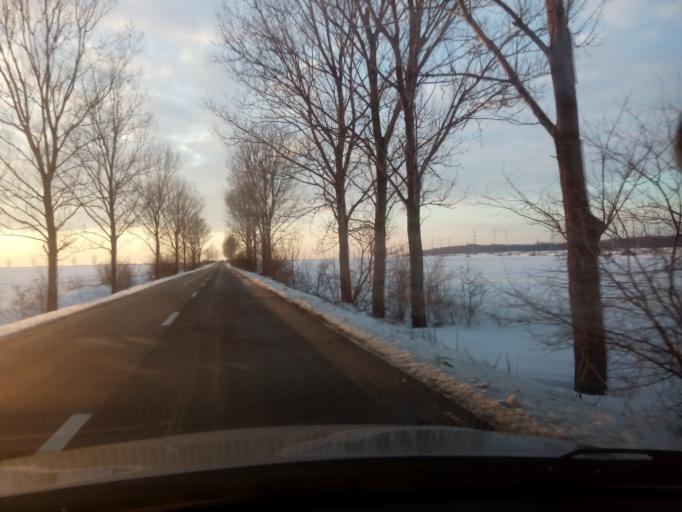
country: RO
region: Calarasi
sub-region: Comuna Luica
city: Luica
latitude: 44.2253
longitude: 26.5592
